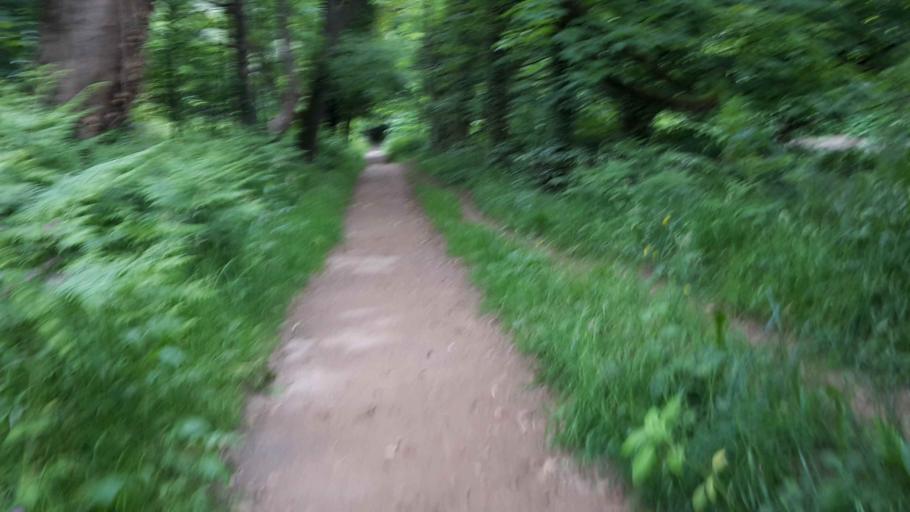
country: GB
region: Scotland
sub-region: South Lanarkshire
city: Uddingston
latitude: 55.8034
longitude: -4.0858
